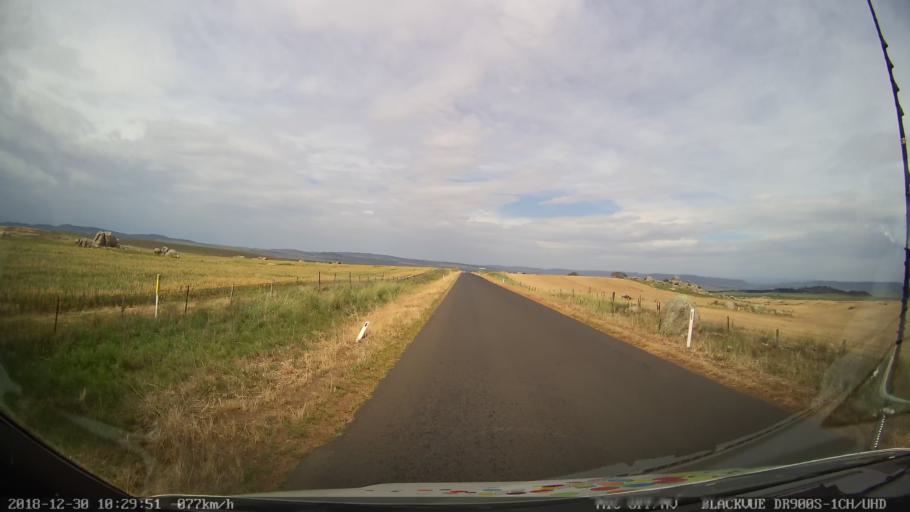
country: AU
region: New South Wales
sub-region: Snowy River
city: Berridale
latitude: -36.5016
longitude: 148.9033
